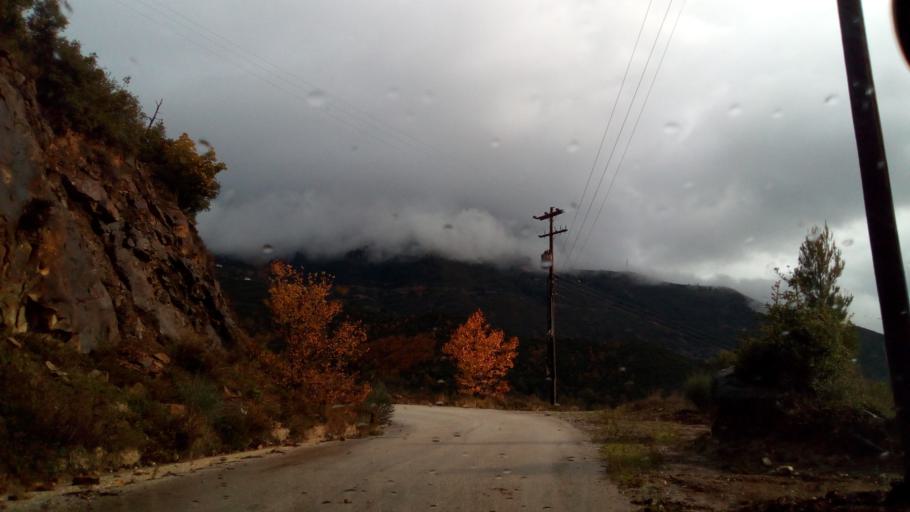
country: GR
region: West Greece
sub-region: Nomos Aitolias kai Akarnanias
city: Thermo
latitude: 38.6739
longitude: 21.8560
